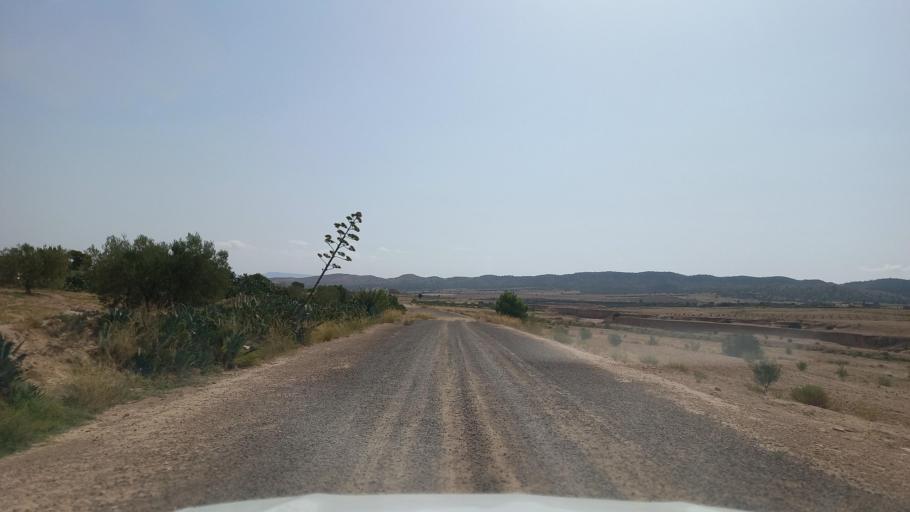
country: TN
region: Al Qasrayn
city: Sbiba
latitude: 35.3940
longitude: 8.9529
